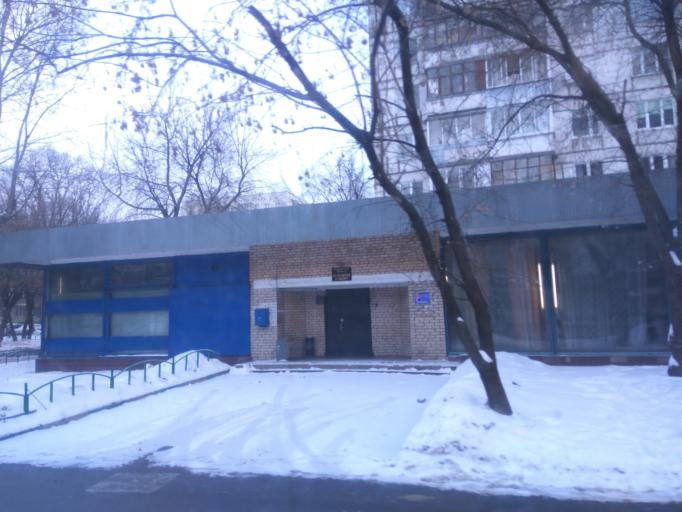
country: RU
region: Moscow
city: Mar'ina Roshcha
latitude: 55.8055
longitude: 37.5731
